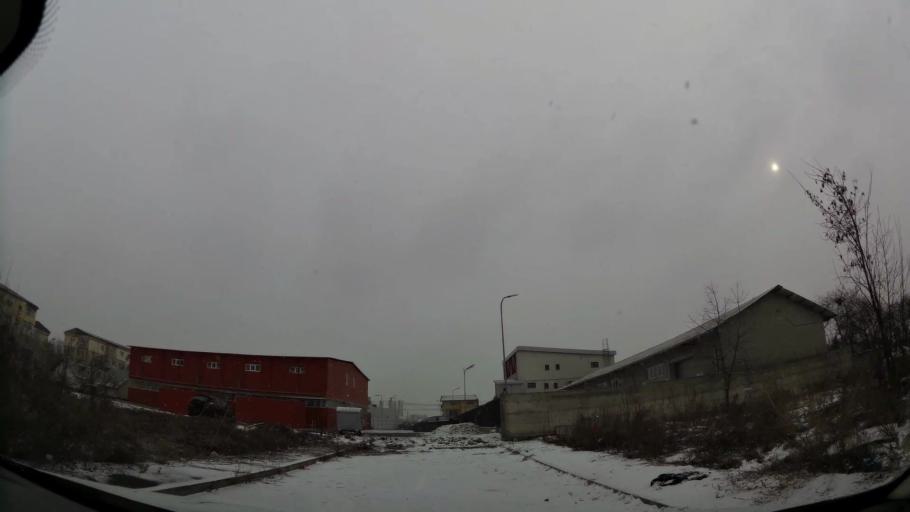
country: RO
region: Dambovita
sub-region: Municipiul Targoviste
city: Targoviste
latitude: 44.9125
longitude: 25.4733
